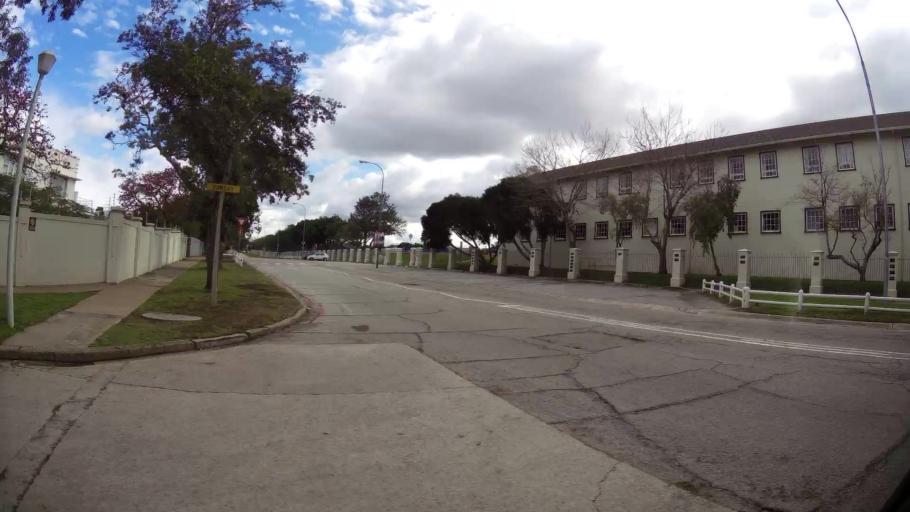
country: ZA
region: Eastern Cape
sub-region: Nelson Mandela Bay Metropolitan Municipality
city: Port Elizabeth
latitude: -33.9626
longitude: 25.5957
